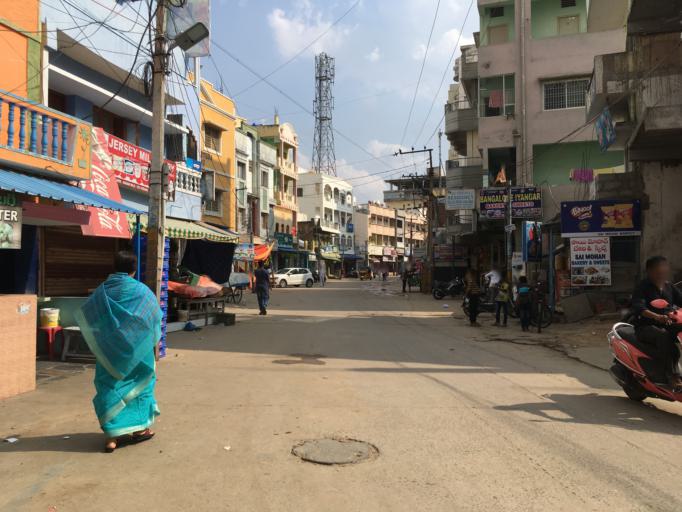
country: IN
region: Andhra Pradesh
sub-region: Anantapur
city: Puttaparthi
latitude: 14.1686
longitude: 77.8110
